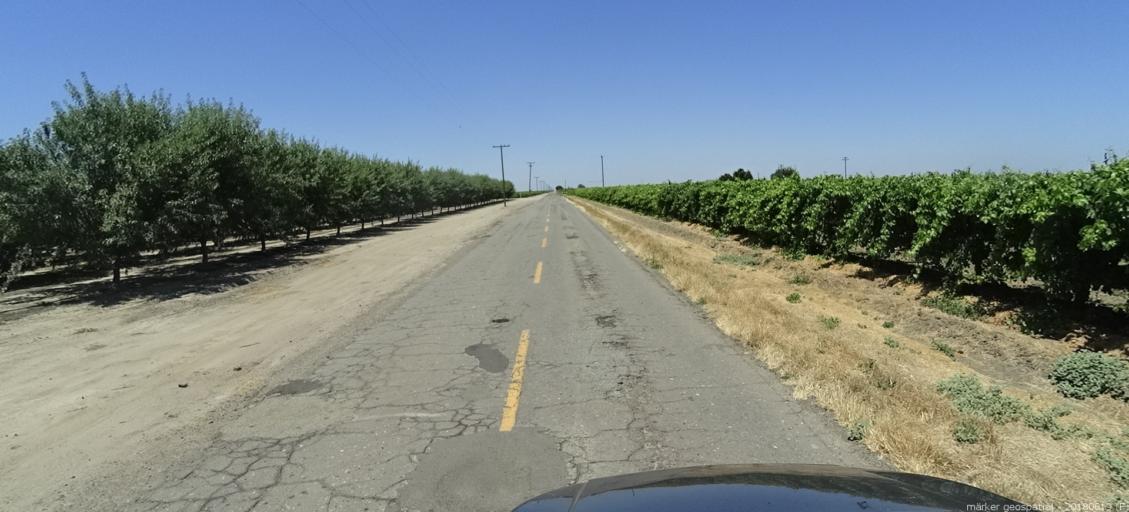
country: US
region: California
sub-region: Madera County
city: Parkwood
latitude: 36.8657
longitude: -120.1219
